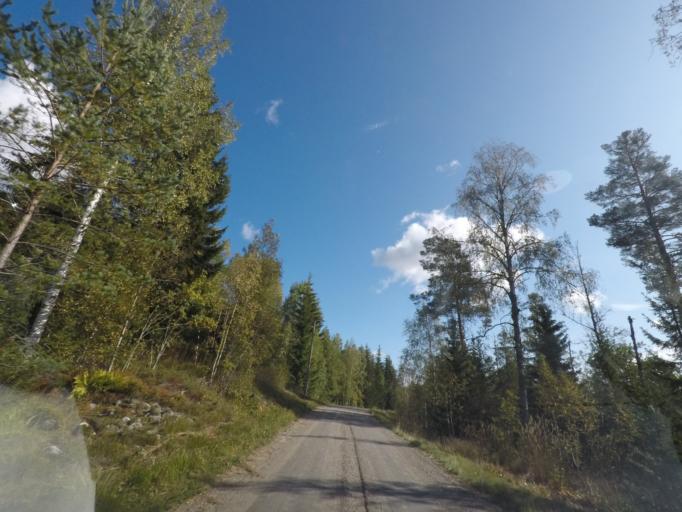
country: SE
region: Vaestmanland
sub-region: Skinnskattebergs Kommun
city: Skinnskatteberg
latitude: 59.8278
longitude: 15.5148
